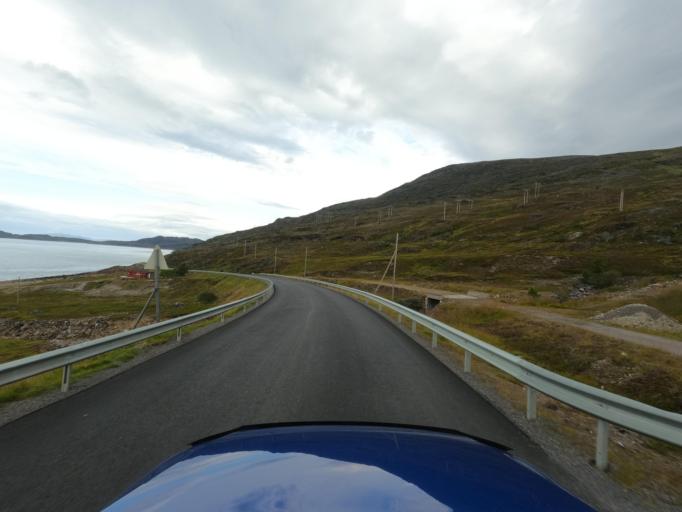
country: NO
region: Finnmark Fylke
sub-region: Hammerfest
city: Rypefjord
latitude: 70.5659
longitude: 23.6996
